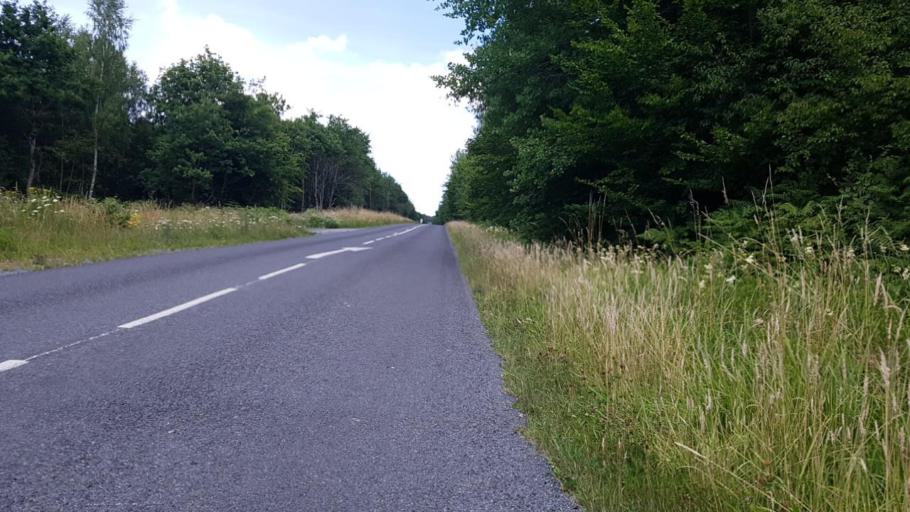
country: FR
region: Picardie
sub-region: Departement de l'Oise
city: Chiry-Ourscamp
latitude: 49.5266
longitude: 2.9839
